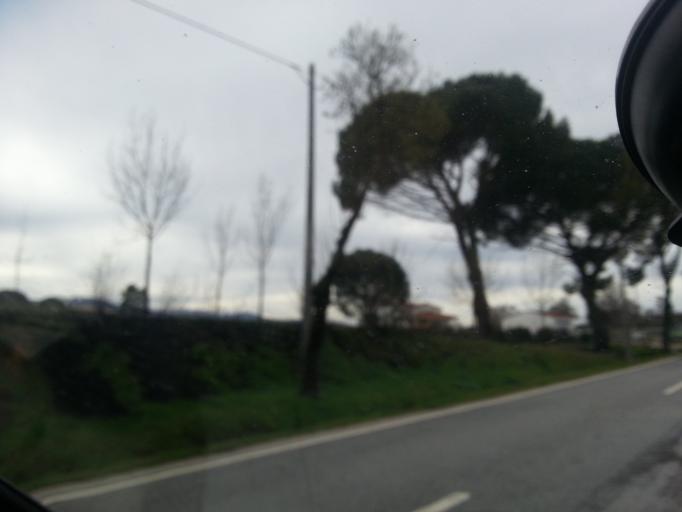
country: PT
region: Guarda
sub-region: Seia
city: Seia
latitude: 40.5077
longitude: -7.6425
